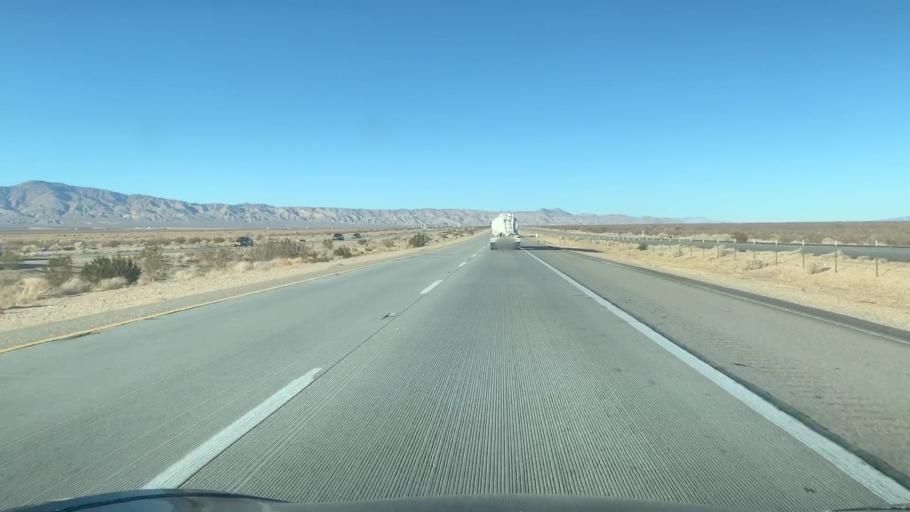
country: US
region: California
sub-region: Kern County
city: Mojave
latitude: 35.0535
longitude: -118.1127
